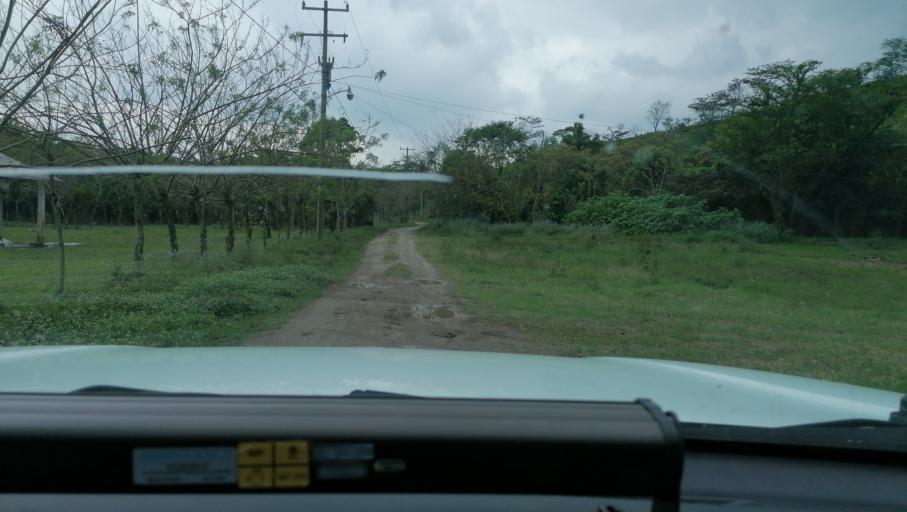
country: MX
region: Chiapas
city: Ixtacomitan
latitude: 17.3691
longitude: -93.1823
